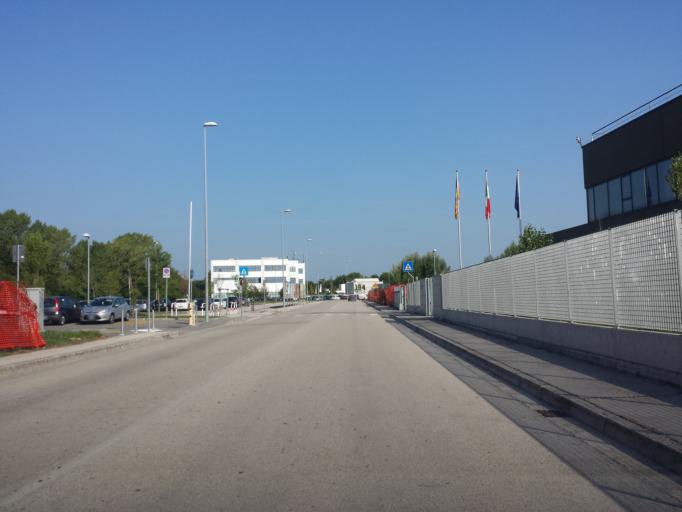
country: IT
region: Veneto
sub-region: Provincia di Vicenza
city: Villaggio Montegrappa
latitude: 45.5264
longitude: 11.5887
